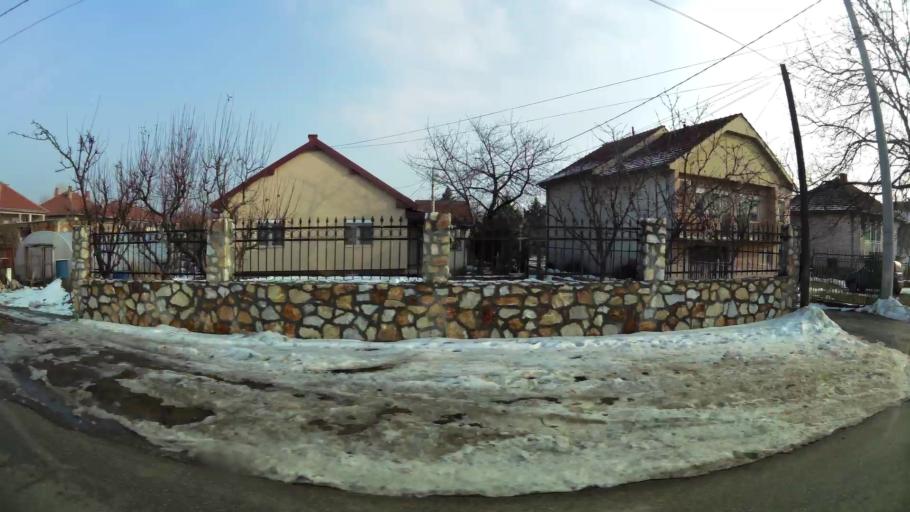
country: MK
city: Miladinovci
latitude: 41.9786
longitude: 21.6454
